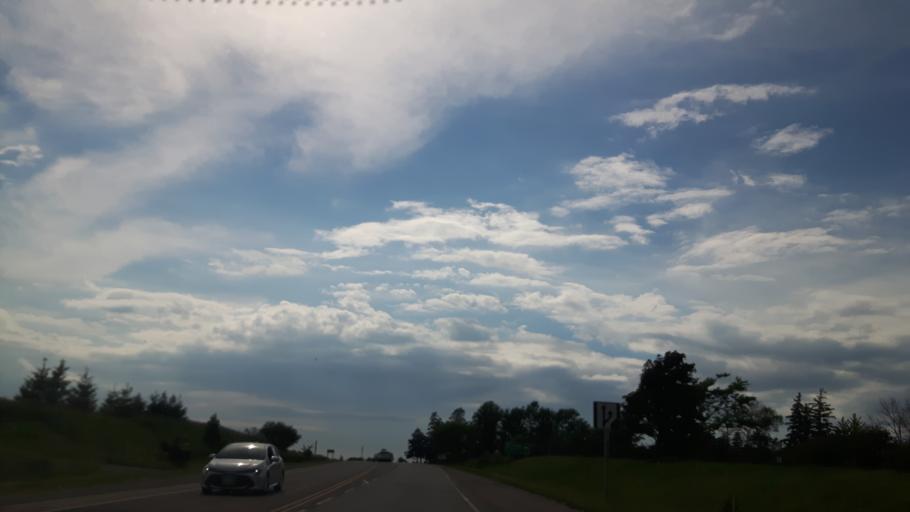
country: CA
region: Ontario
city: South Huron
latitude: 43.1991
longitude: -81.4316
